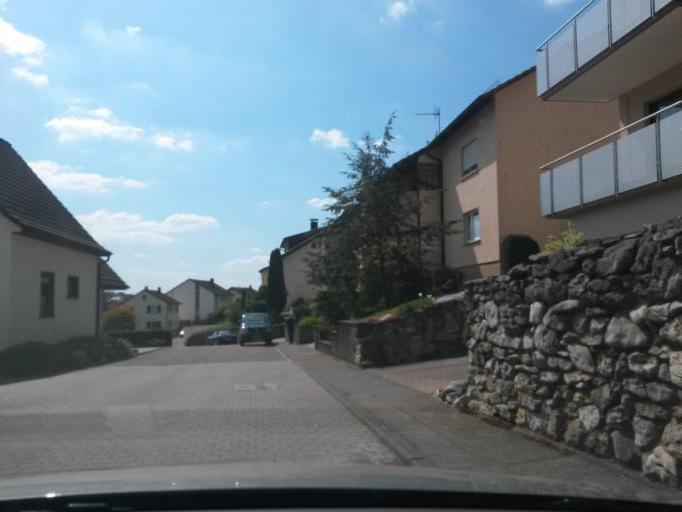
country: DE
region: Baden-Wuerttemberg
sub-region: Karlsruhe Region
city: Birkenfeld
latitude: 48.8979
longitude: 8.6059
